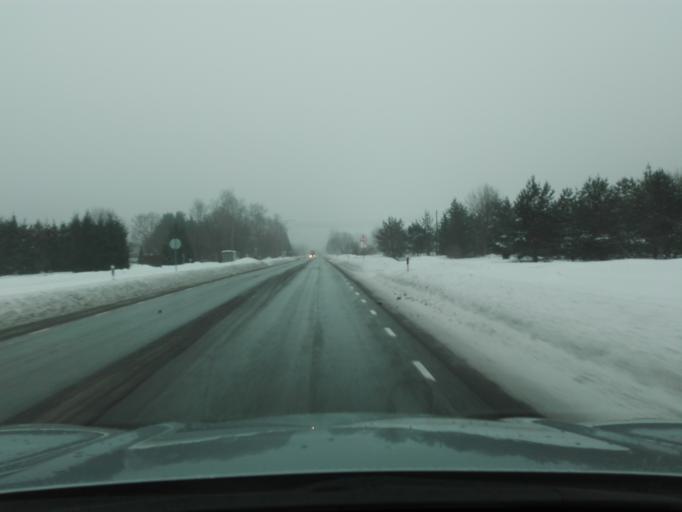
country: EE
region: Harju
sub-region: Kiili vald
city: Kiili
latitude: 59.3416
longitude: 24.7740
